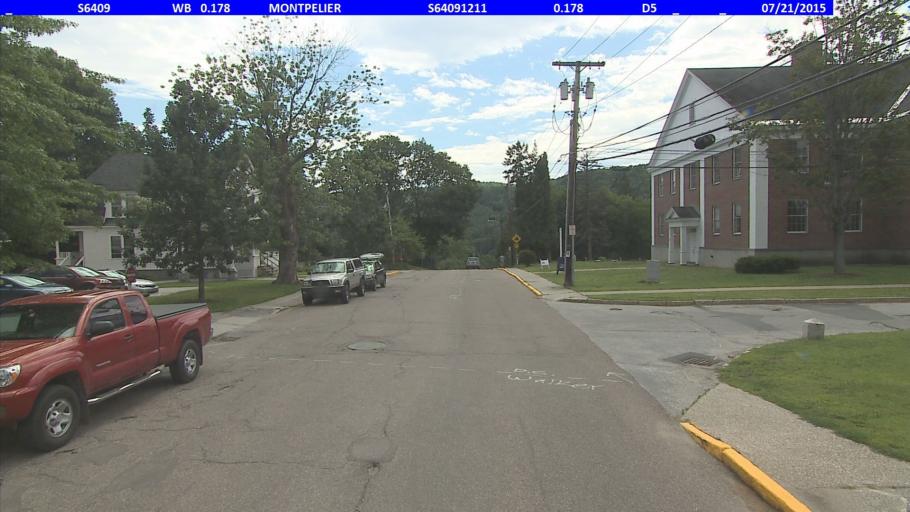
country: US
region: Vermont
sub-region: Washington County
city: Montpelier
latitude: 44.2548
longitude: -72.5669
